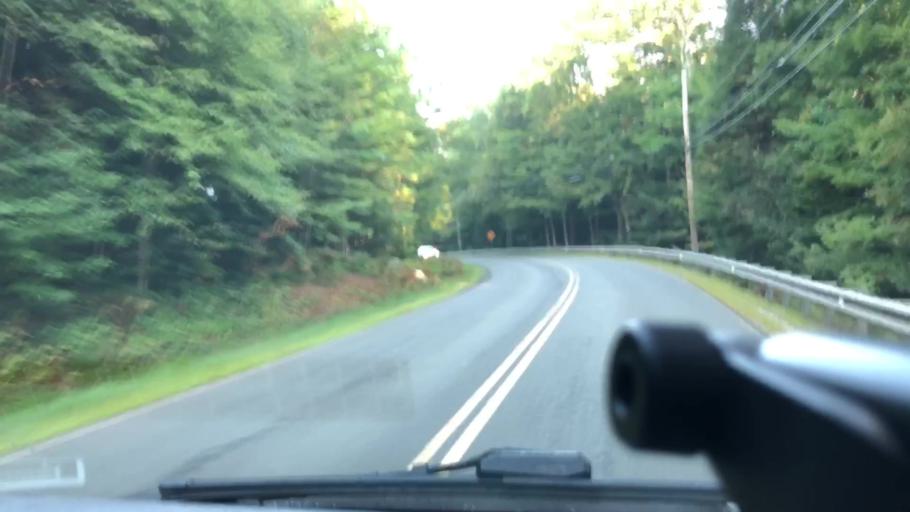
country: US
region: Massachusetts
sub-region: Franklin County
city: Ashfield
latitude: 42.5096
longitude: -72.8336
